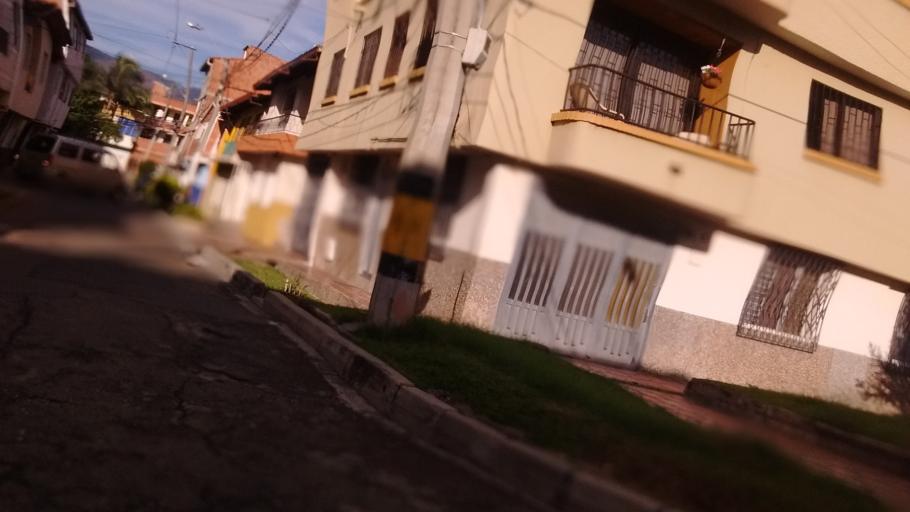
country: CO
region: Antioquia
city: Medellin
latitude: 6.2567
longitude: -75.6083
